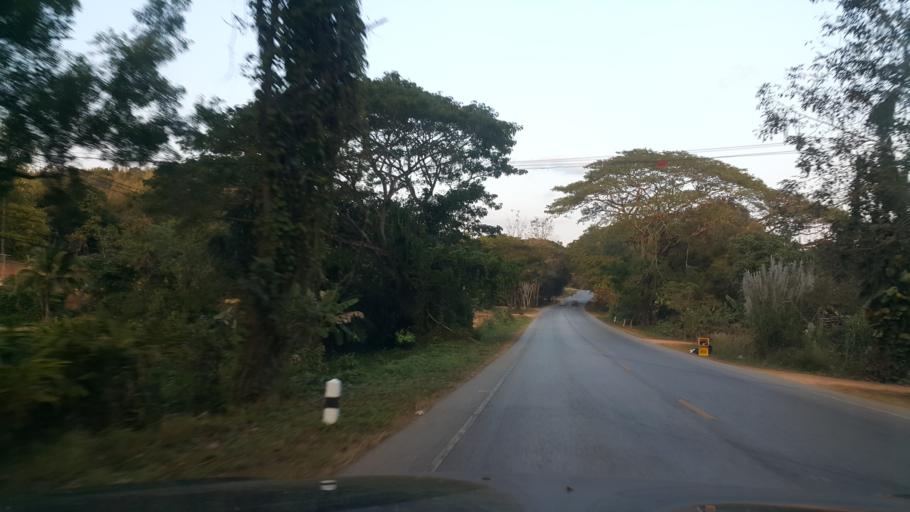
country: TH
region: Loei
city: Loei
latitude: 17.4746
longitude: 101.6001
